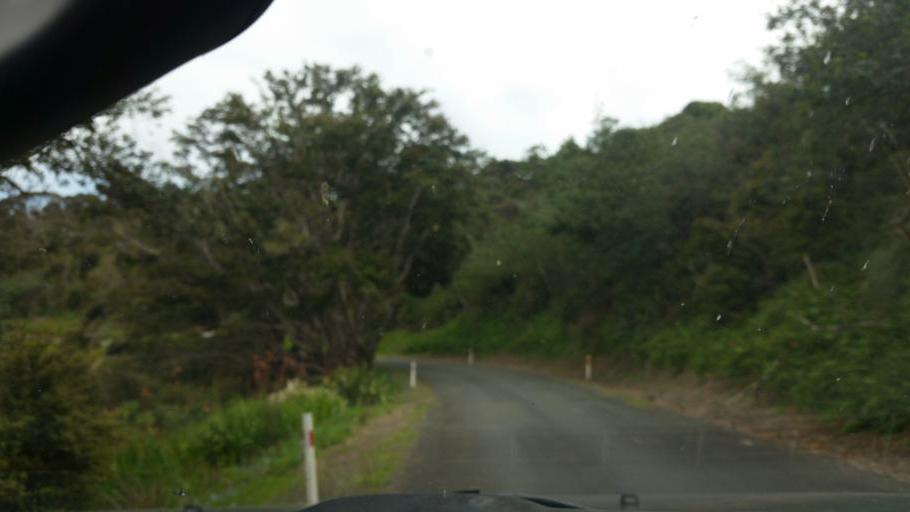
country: NZ
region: Northland
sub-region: Kaipara District
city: Dargaville
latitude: -35.8007
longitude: 173.6274
